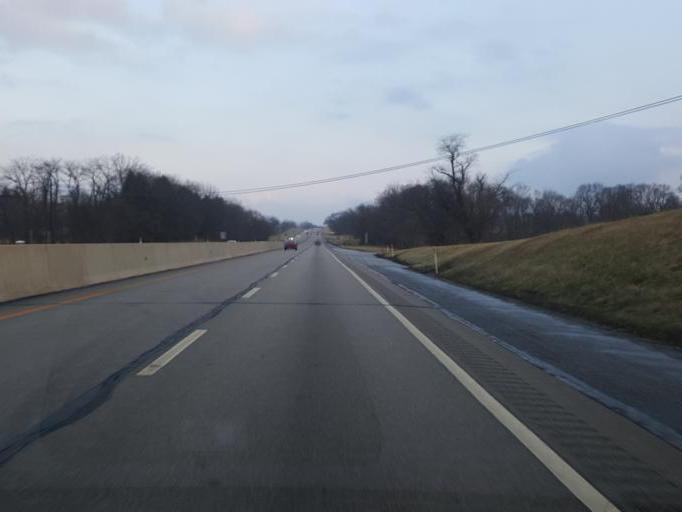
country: US
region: Pennsylvania
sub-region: Cumberland County
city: Mechanicsburg
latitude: 40.2164
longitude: -77.0867
